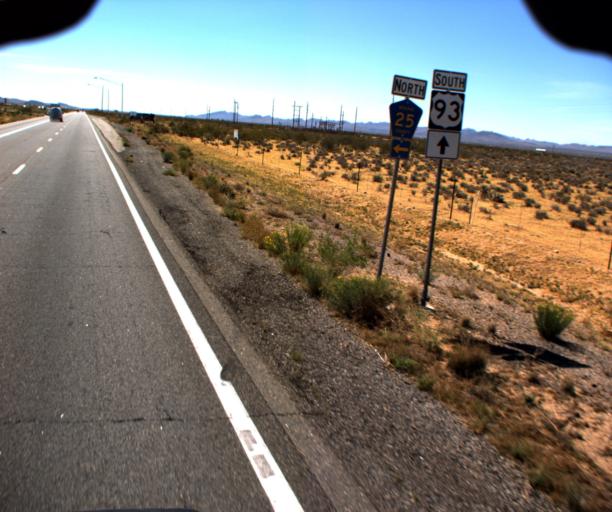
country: US
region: Arizona
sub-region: Mohave County
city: Dolan Springs
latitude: 35.5356
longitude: -114.3568
